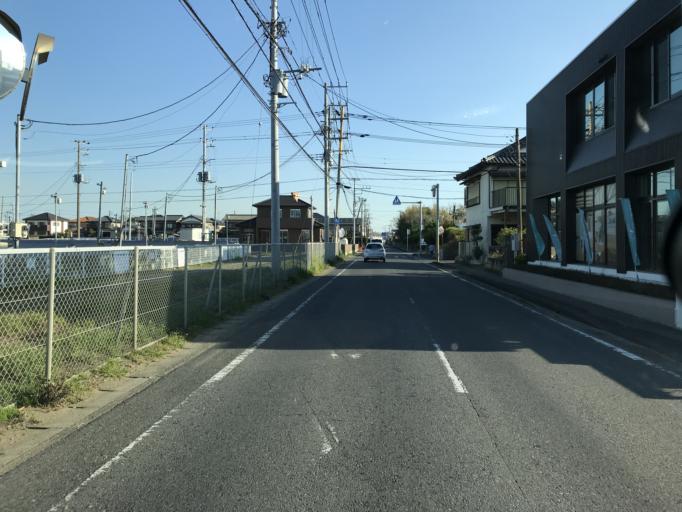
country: JP
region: Chiba
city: Asahi
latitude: 35.7232
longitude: 140.6847
